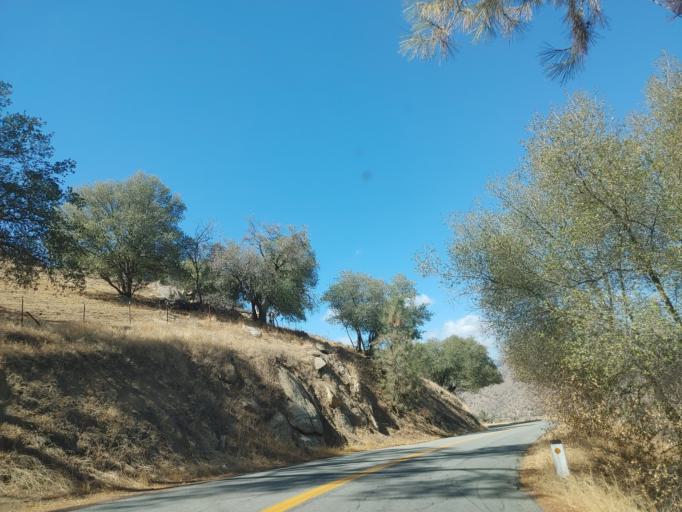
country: US
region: California
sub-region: Kern County
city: Golden Hills
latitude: 35.1797
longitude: -118.5136
